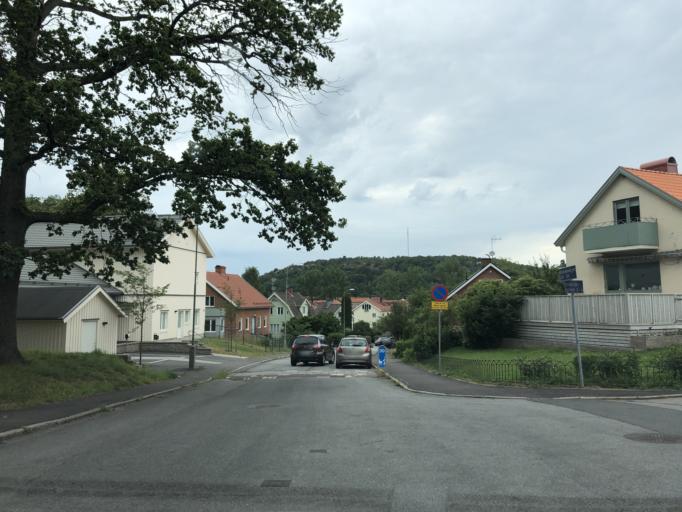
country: SE
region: Vaestra Goetaland
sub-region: Goteborg
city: Majorna
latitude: 57.7267
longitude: 11.9243
